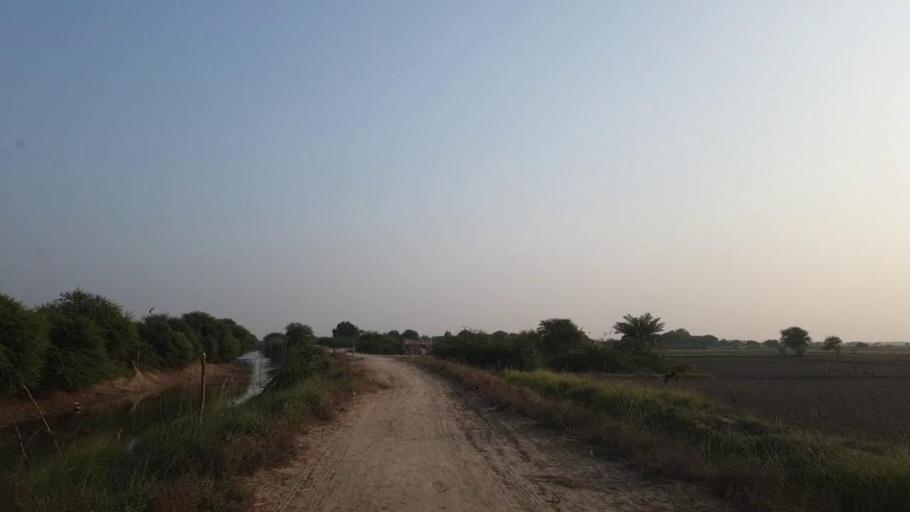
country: PK
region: Sindh
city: Kario
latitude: 24.8661
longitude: 68.6221
